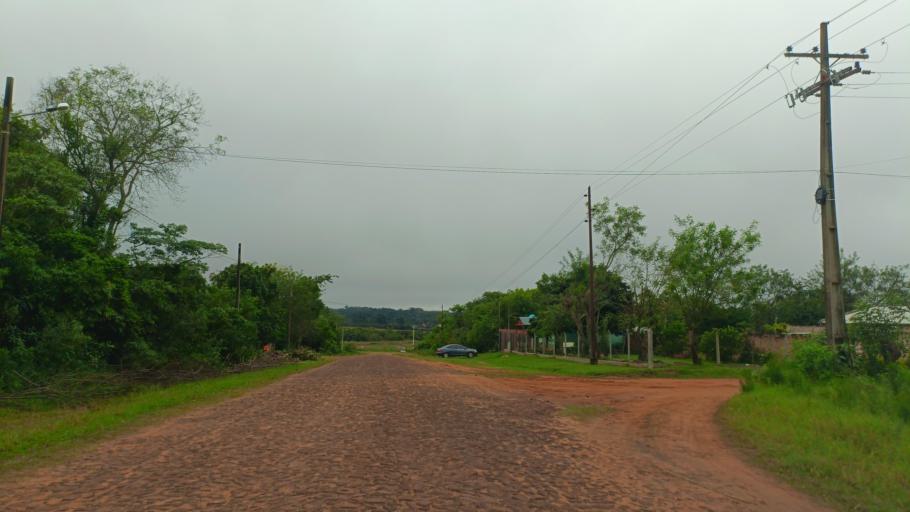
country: PY
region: Misiones
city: Santa Maria
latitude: -26.8727
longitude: -57.0086
